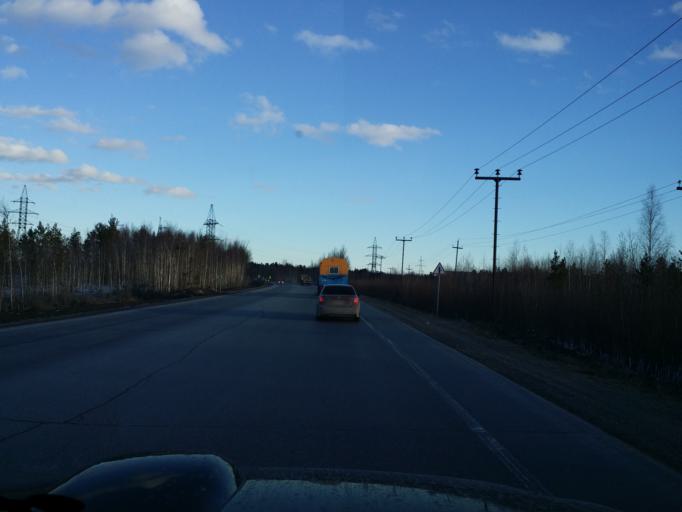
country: RU
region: Khanty-Mansiyskiy Avtonomnyy Okrug
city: Nizhnevartovsk
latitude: 61.0290
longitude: 76.3634
